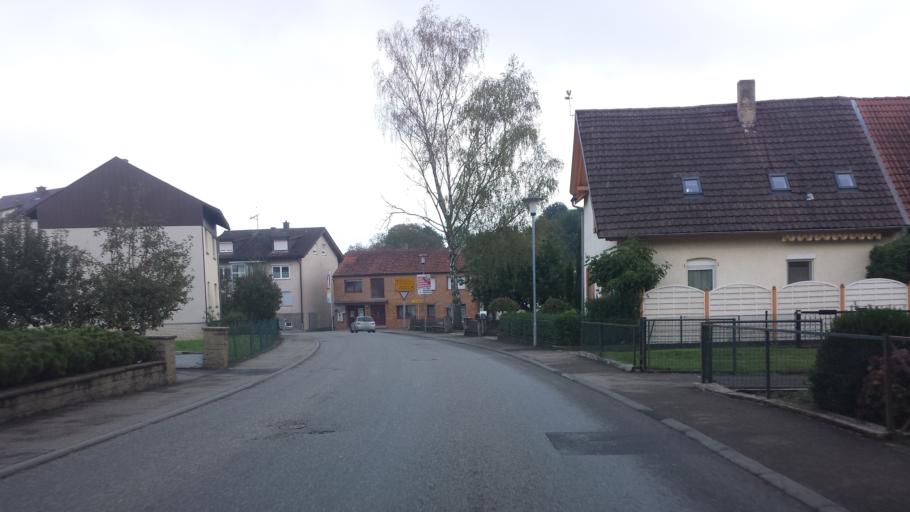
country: DE
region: Baden-Wuerttemberg
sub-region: Regierungsbezirk Stuttgart
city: Kirchardt
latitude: 49.2027
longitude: 8.9869
